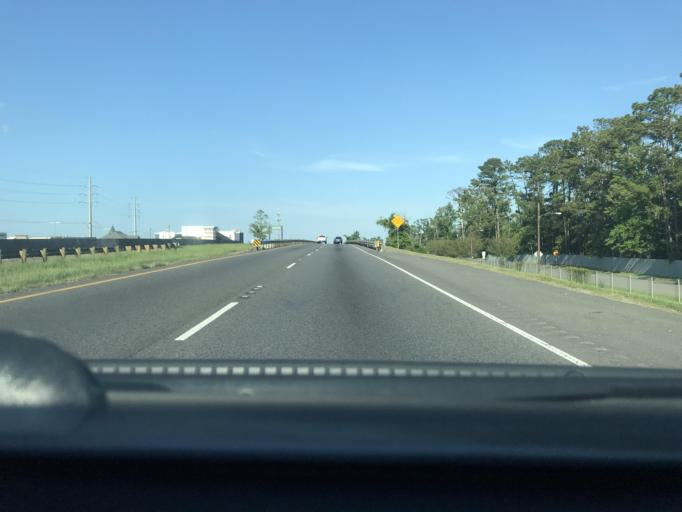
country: US
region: Louisiana
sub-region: Calcasieu Parish
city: Prien
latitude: 30.1968
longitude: -93.2431
